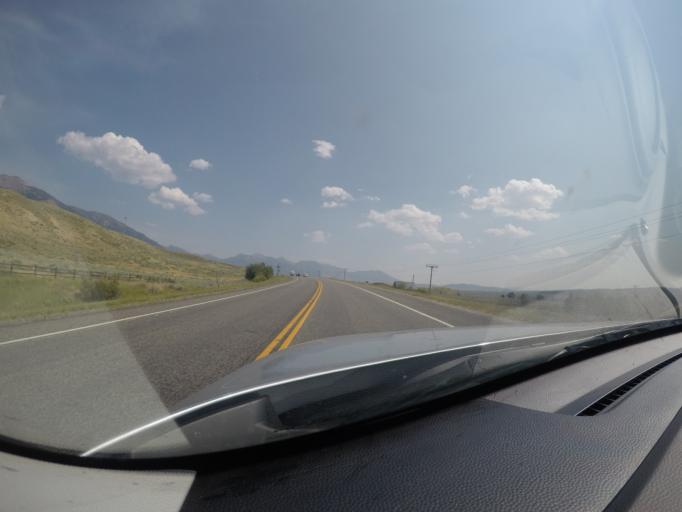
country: US
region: Montana
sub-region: Gallatin County
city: Big Sky
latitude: 44.8555
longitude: -111.5430
